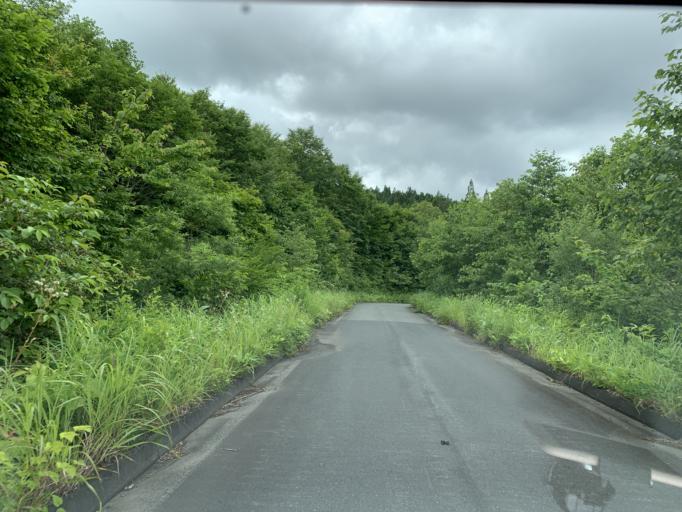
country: JP
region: Iwate
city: Ichinoseki
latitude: 38.9355
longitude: 140.8786
